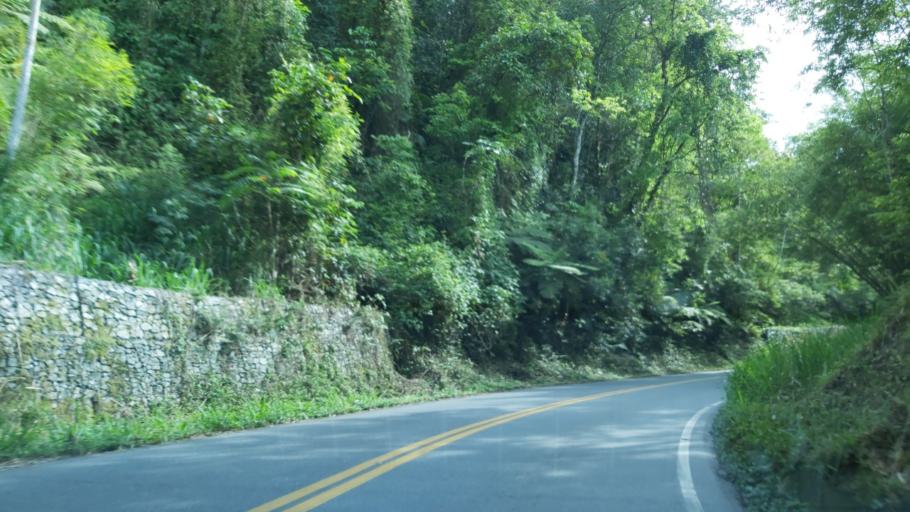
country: BR
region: Sao Paulo
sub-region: Juquia
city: Juquia
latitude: -24.1082
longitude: -47.6258
